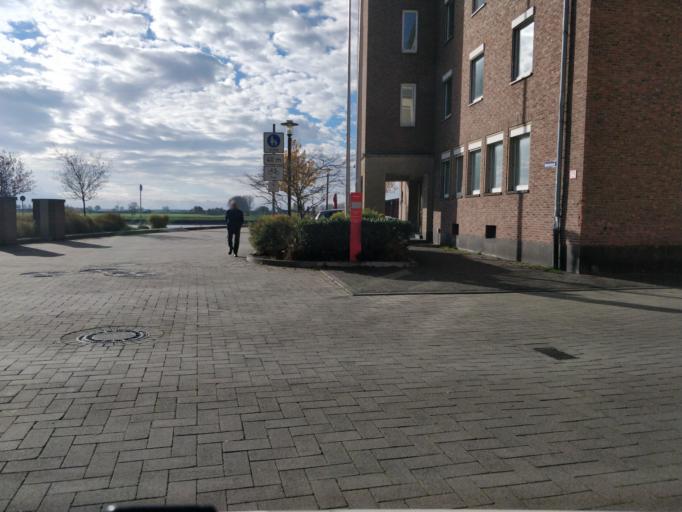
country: DE
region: North Rhine-Westphalia
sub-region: Regierungsbezirk Dusseldorf
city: Emmerich
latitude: 51.8300
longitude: 6.2469
